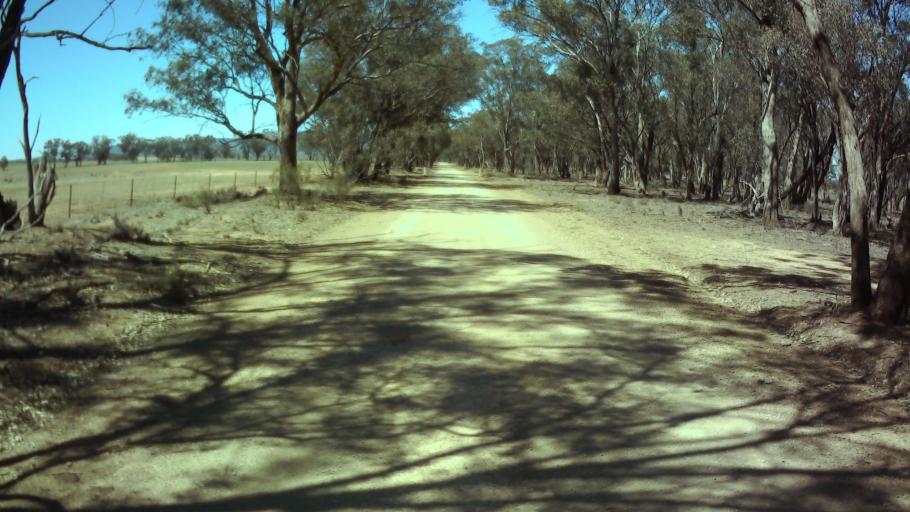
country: AU
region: New South Wales
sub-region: Weddin
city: Grenfell
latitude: -33.9011
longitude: 148.0827
